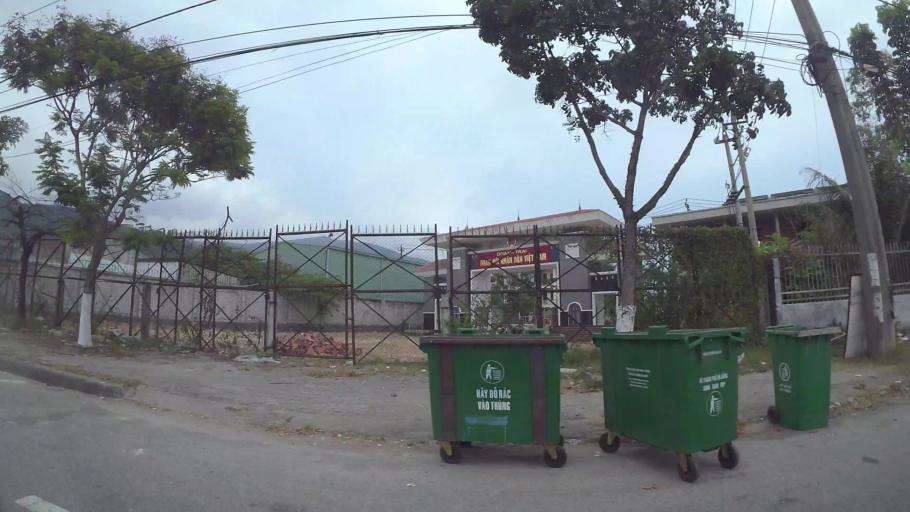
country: VN
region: Da Nang
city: Da Nang
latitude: 16.1028
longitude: 108.2476
